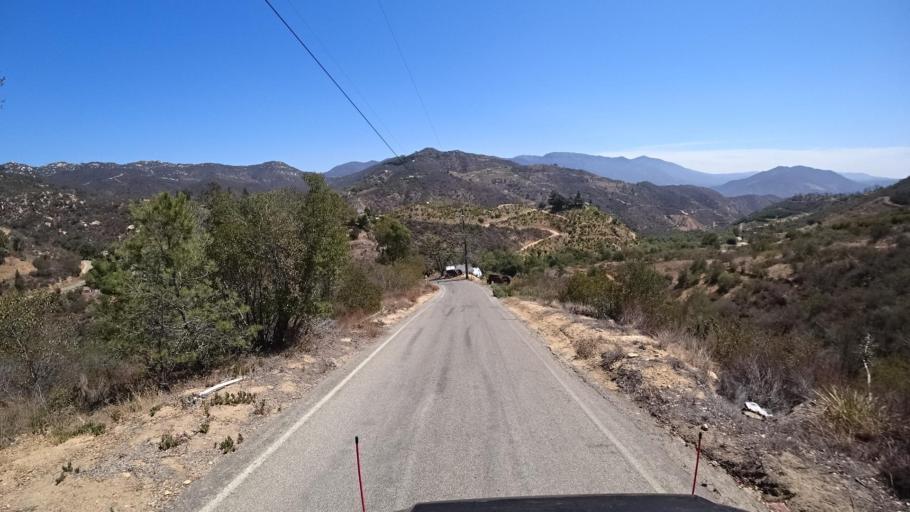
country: US
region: California
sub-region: San Diego County
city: Rainbow
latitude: 33.3855
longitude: -117.1168
